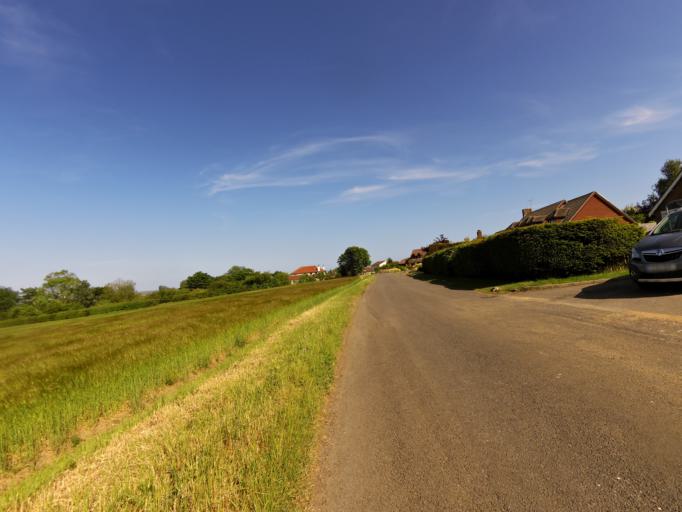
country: GB
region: England
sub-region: Suffolk
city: Felixstowe
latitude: 51.9782
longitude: 1.3760
